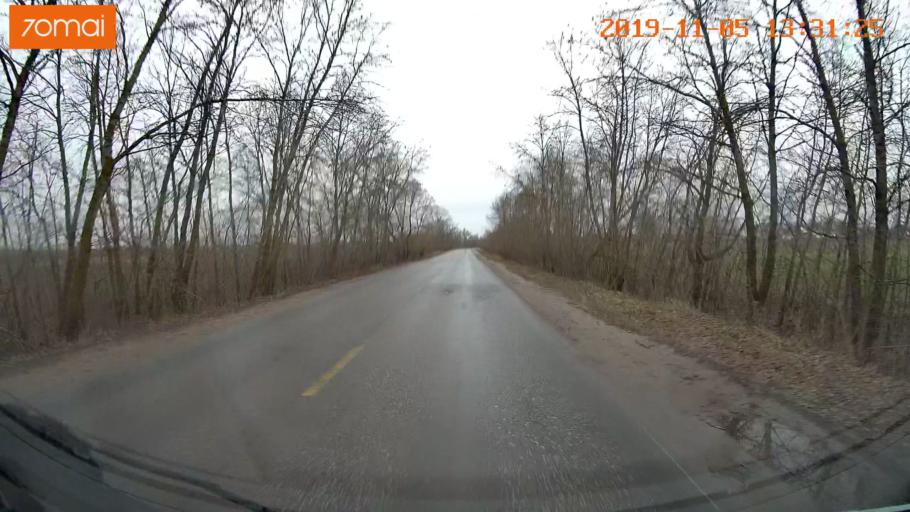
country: RU
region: Ivanovo
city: Shuya
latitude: 56.8756
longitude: 41.3932
